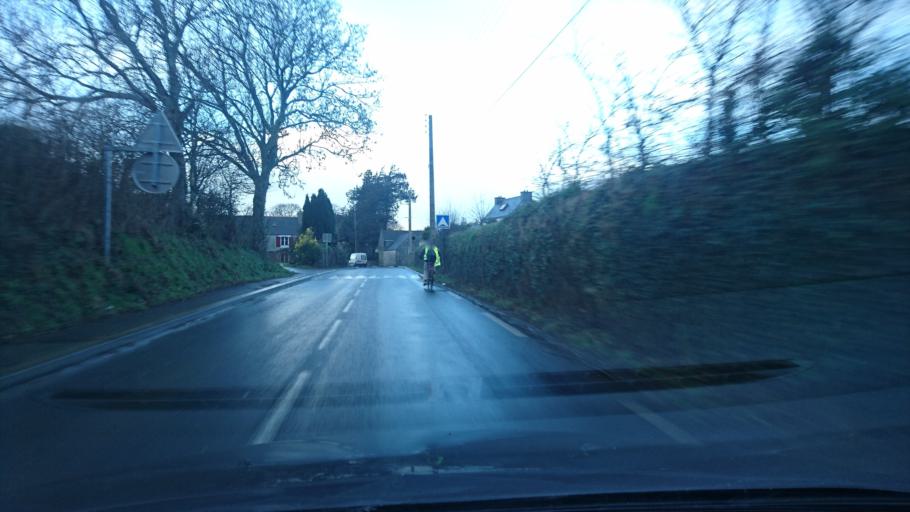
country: FR
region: Brittany
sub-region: Departement du Finistere
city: Guilers
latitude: 48.3975
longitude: -4.5393
